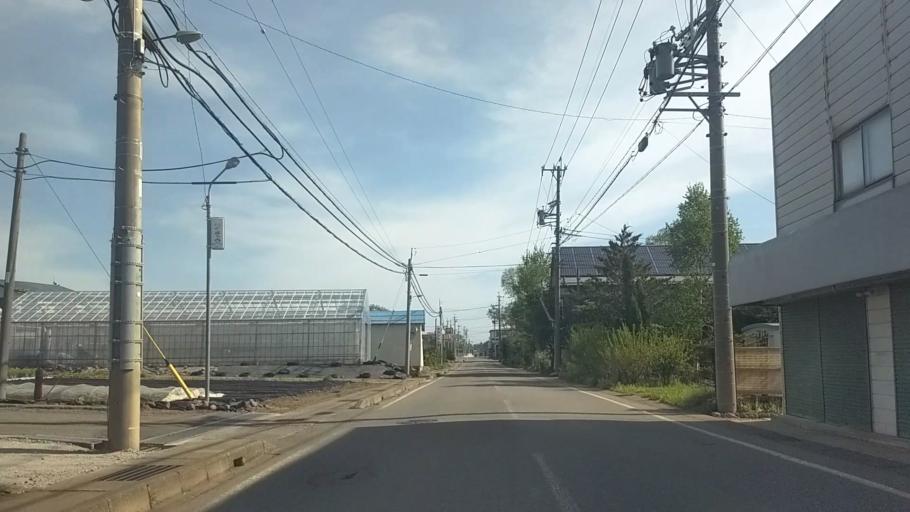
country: JP
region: Yamanashi
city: Nirasaki
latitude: 35.9529
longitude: 138.4730
